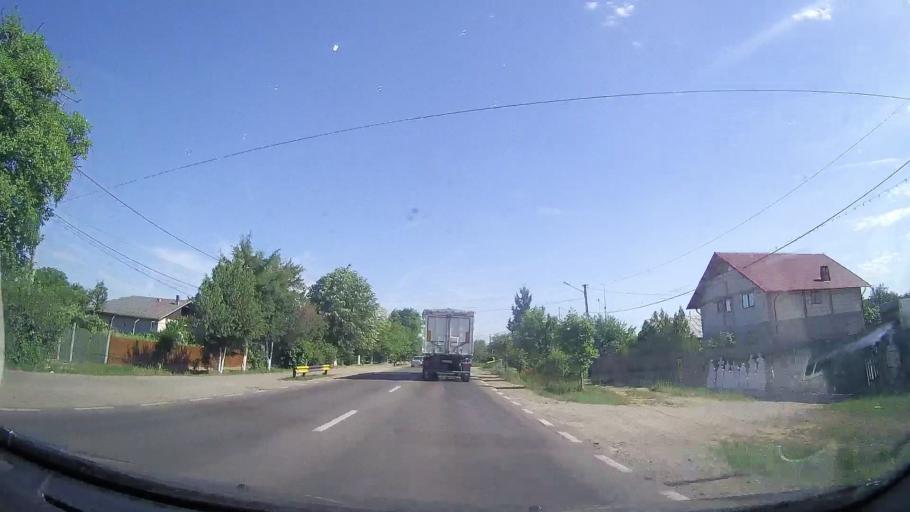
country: RO
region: Prahova
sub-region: Comuna Lipanesti
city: Sipotu
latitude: 45.0340
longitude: 26.0173
